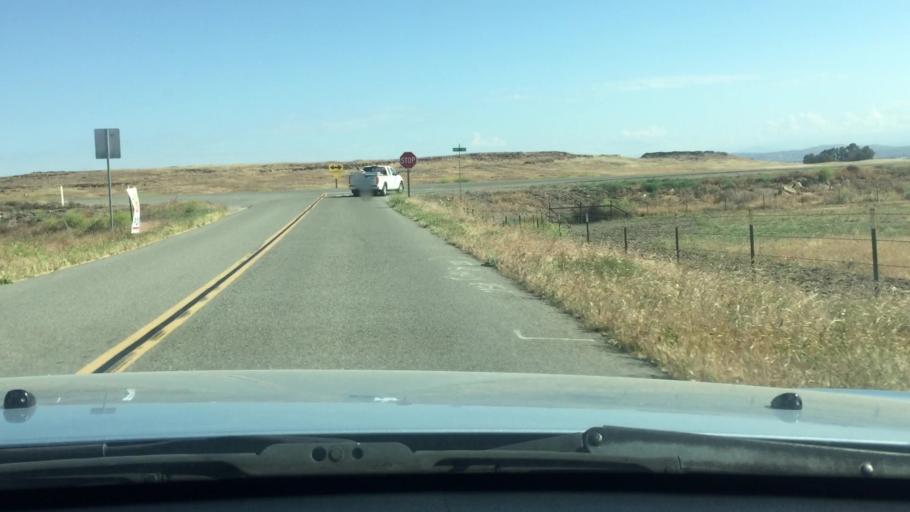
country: US
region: California
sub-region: Madera County
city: Bonadelle Ranchos-Madera Ranchos
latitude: 37.0097
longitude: -119.8576
